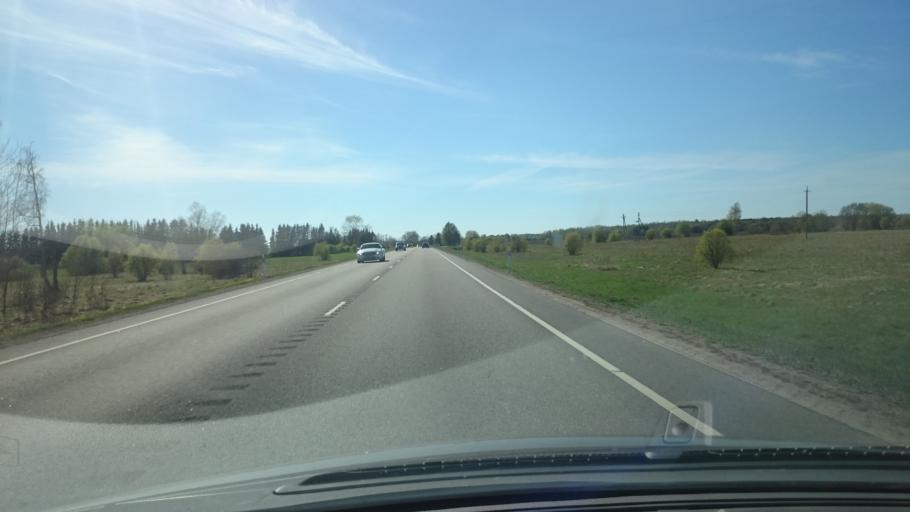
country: EE
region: Ida-Virumaa
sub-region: Kohtla-Jaerve linn
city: Kohtla-Jarve
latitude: 59.4211
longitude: 27.2065
